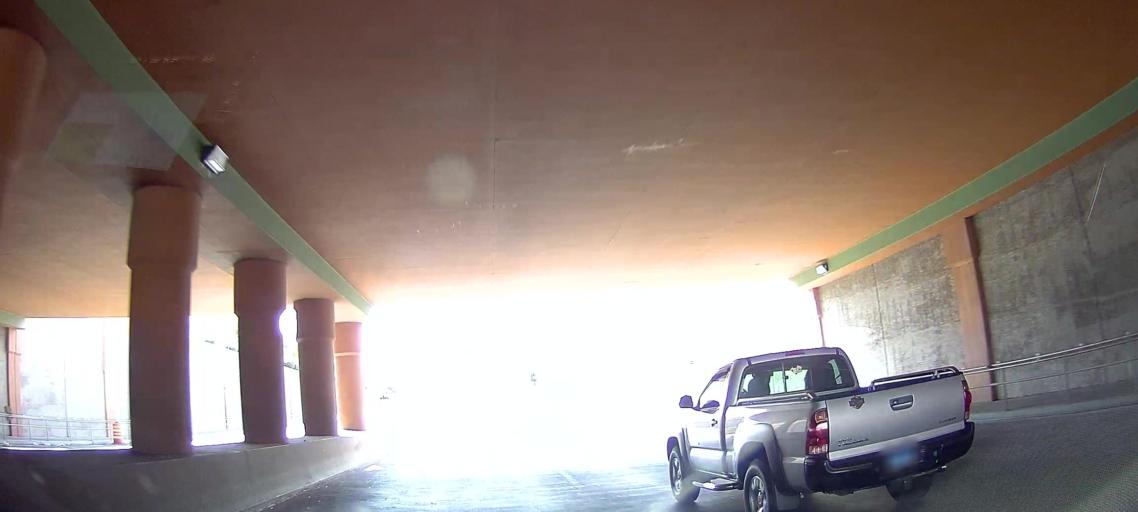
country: US
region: Nevada
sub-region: Clark County
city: Las Vegas
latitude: 36.1664
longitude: -115.1514
